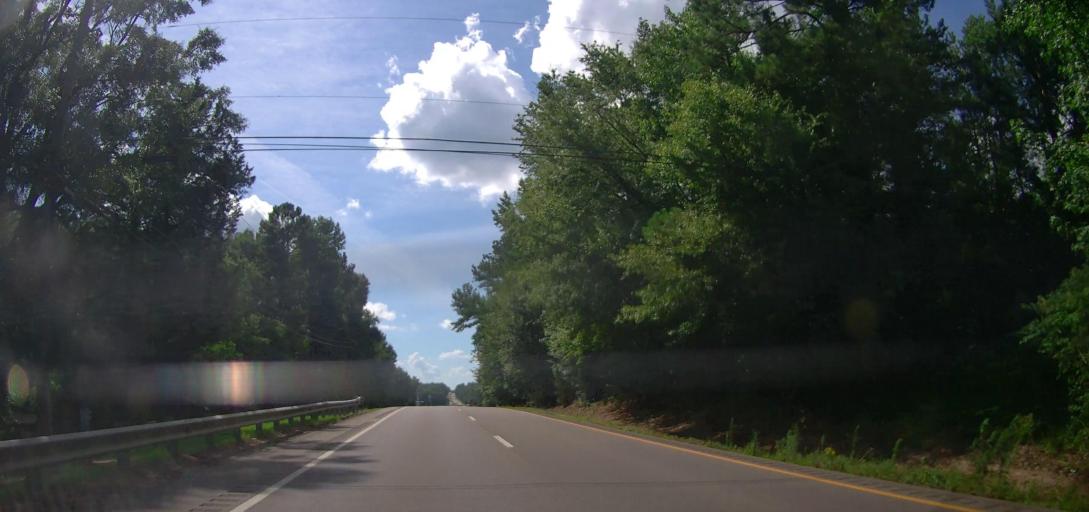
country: US
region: Alabama
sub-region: Tuscaloosa County
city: Northport
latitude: 33.2427
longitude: -87.6674
